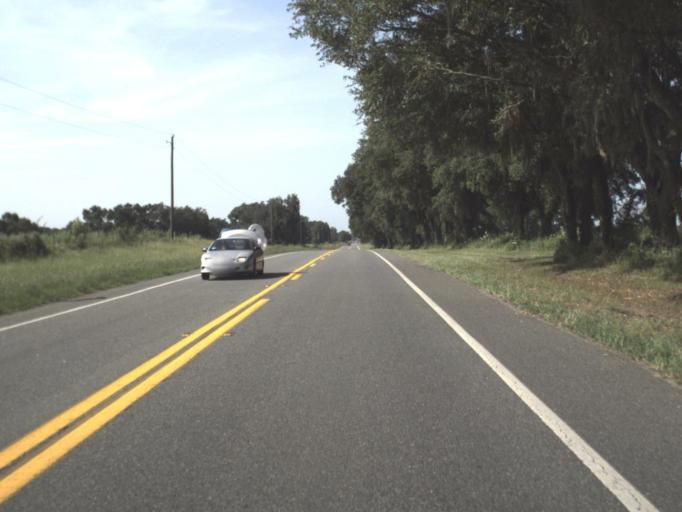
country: US
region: Florida
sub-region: Alachua County
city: High Springs
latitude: 29.9511
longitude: -82.7133
